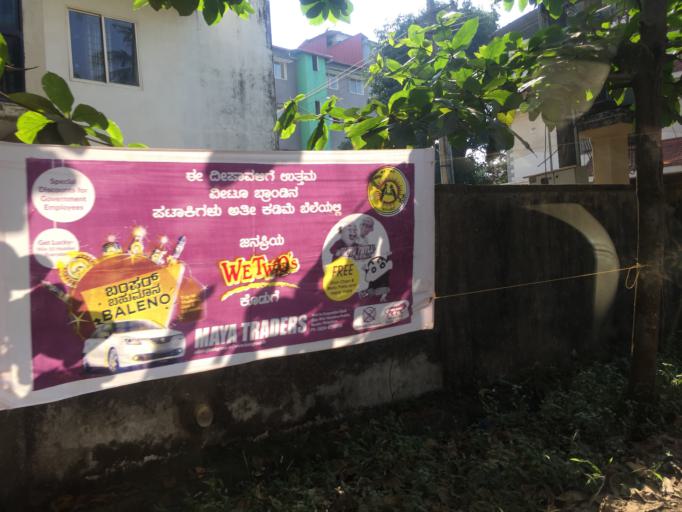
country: IN
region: Karnataka
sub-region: Dakshina Kannada
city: Ullal
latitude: 12.8450
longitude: 74.8438
